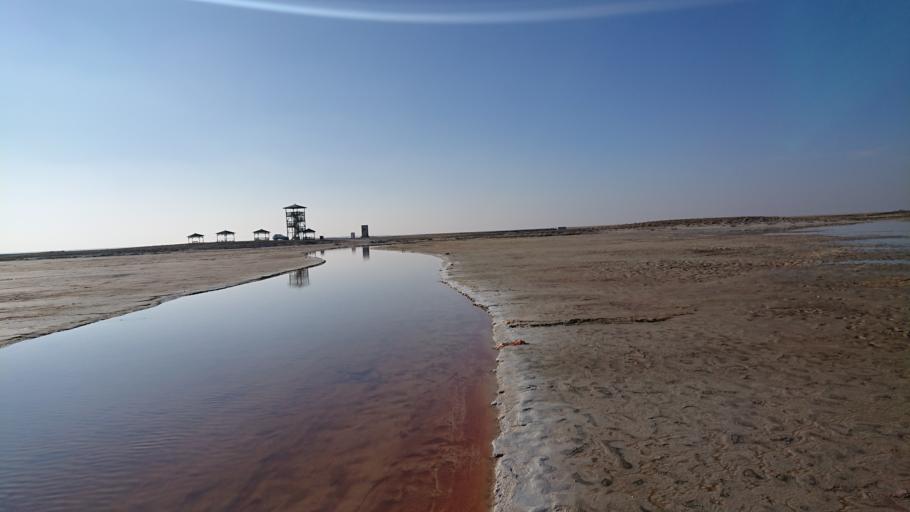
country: TR
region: Aksaray
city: Eskil
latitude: 38.4258
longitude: 33.5034
